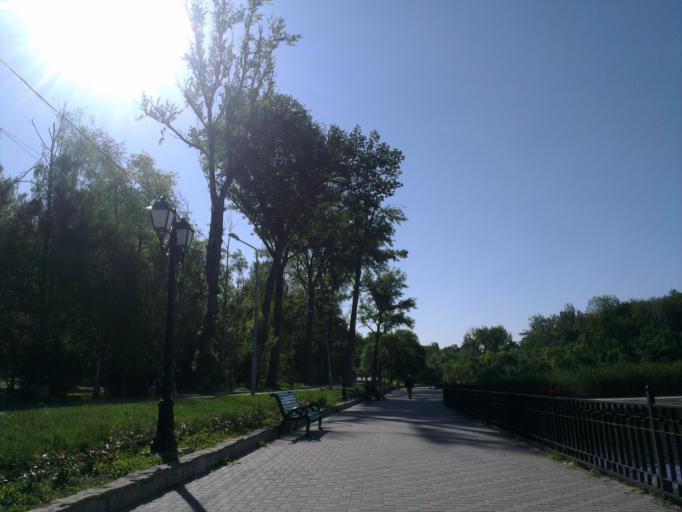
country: MD
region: Chisinau
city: Chisinau
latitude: 47.0196
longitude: 28.8173
